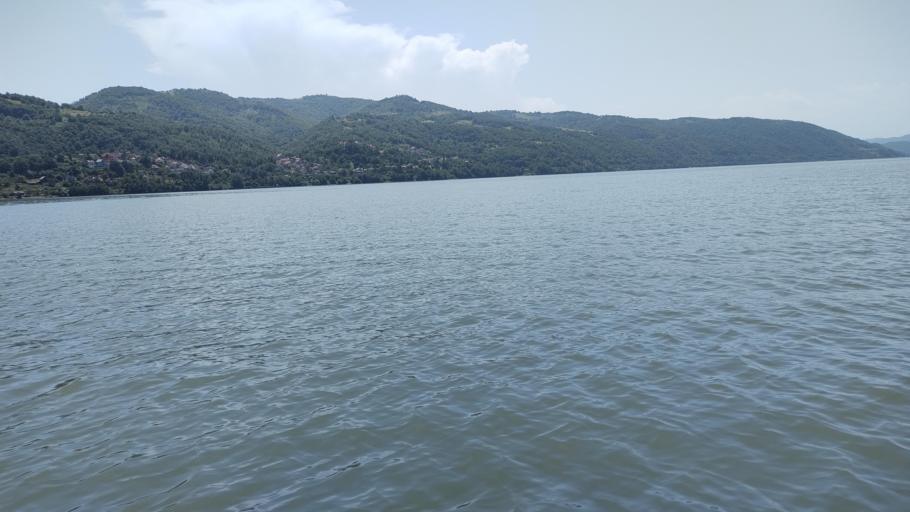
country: RO
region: Mehedinti
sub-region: Comuna Svinita
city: Svinita
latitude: 44.5083
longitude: 22.1943
